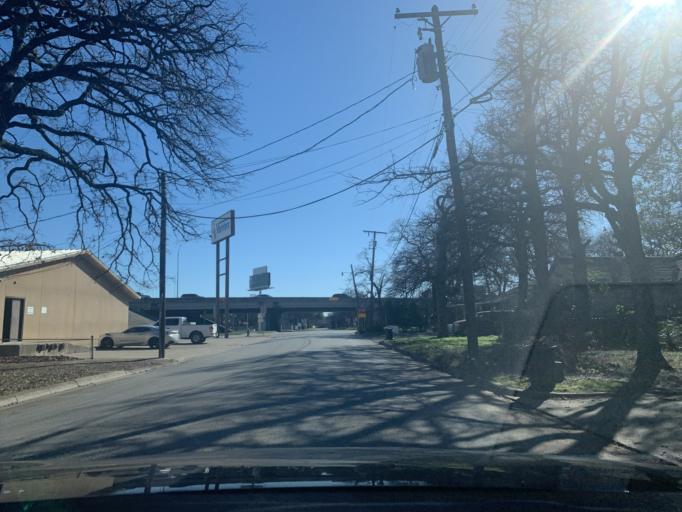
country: US
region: Texas
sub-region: Tarrant County
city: Haltom City
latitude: 32.7805
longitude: -97.2785
